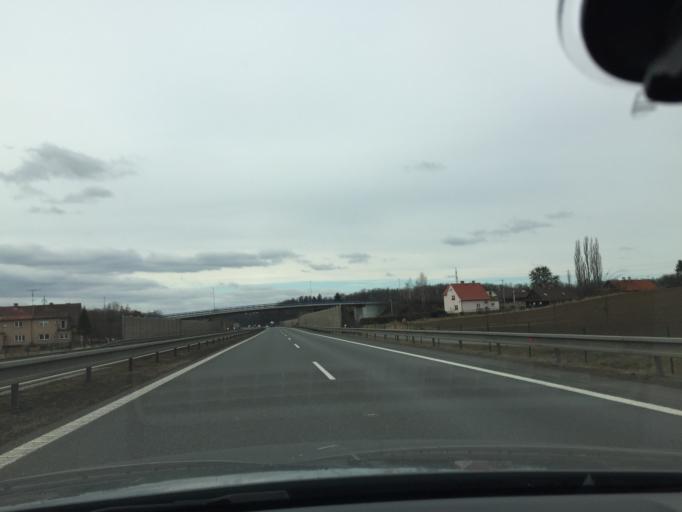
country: CZ
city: Dobra
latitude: 49.6777
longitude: 18.4097
